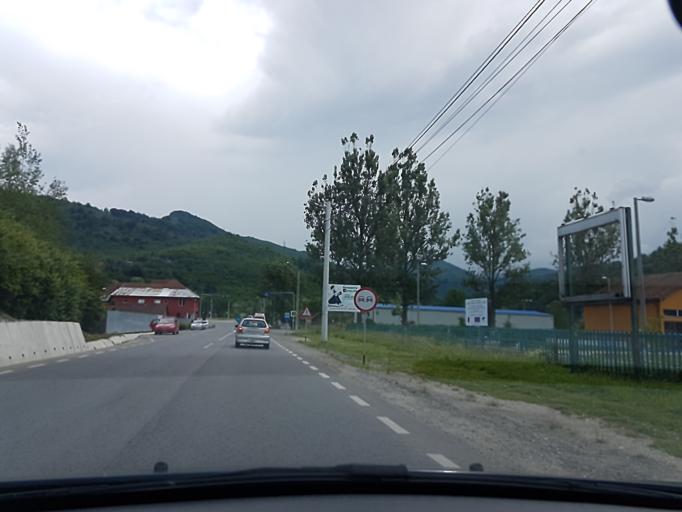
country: RO
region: Hunedoara
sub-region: Comuna Aninoasa
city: Iscroni
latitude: 45.3718
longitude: 23.3629
